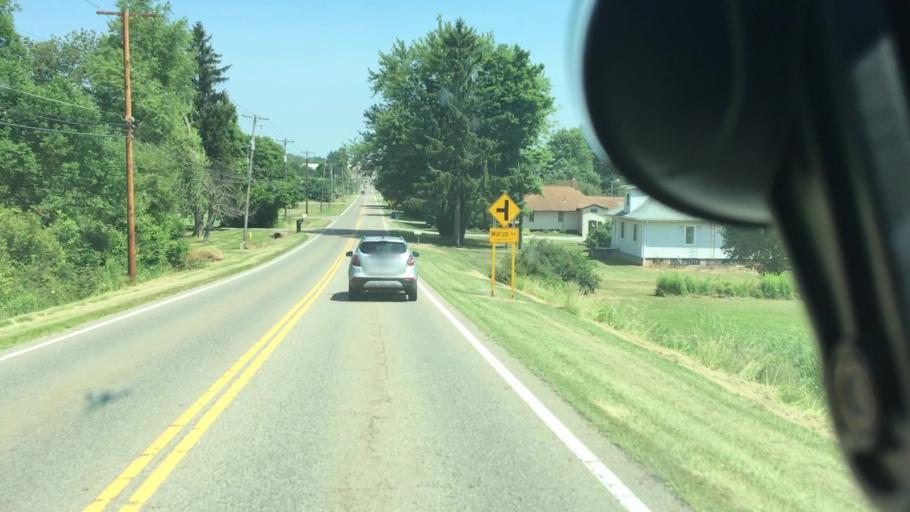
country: US
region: Ohio
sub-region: Columbiana County
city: Salem
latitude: 40.8860
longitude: -80.8570
